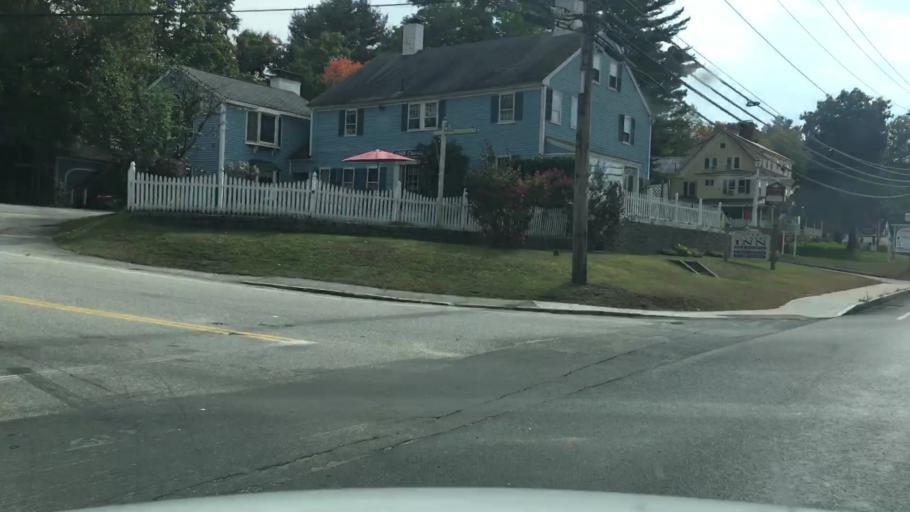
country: US
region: New Hampshire
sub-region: Carroll County
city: North Conway
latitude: 44.0442
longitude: -71.1246
